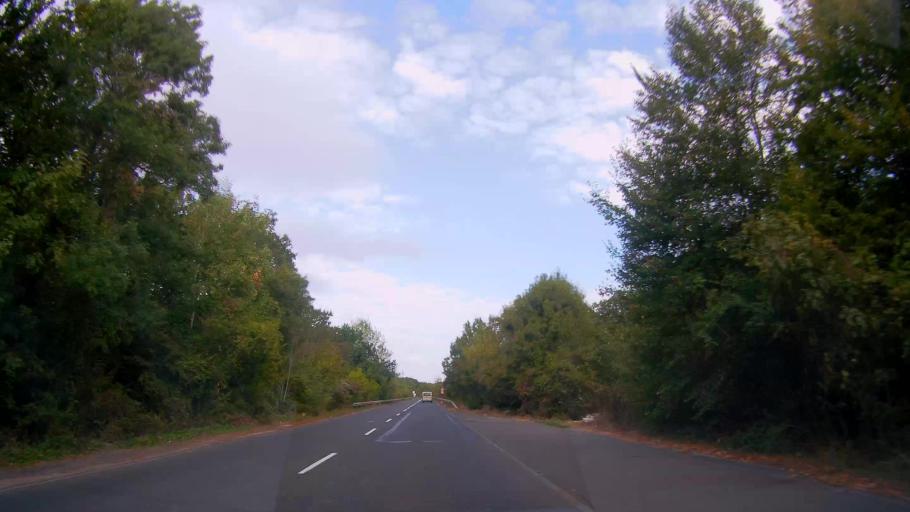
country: BG
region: Burgas
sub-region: Obshtina Primorsko
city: Primorsko
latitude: 42.3348
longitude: 27.7226
